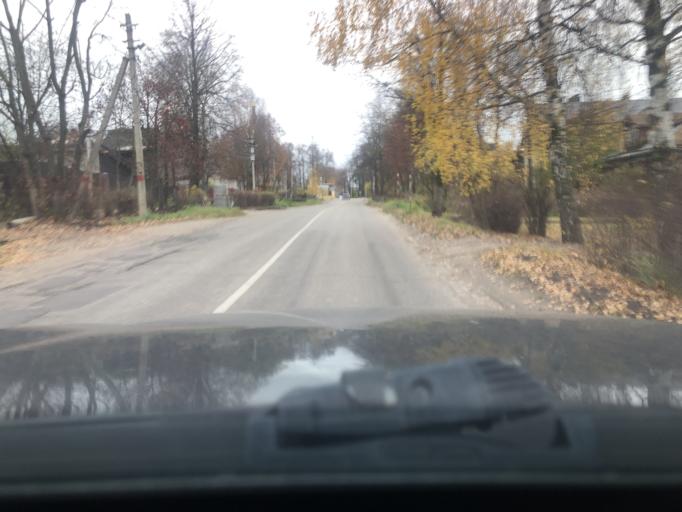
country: RU
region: Moskovskaya
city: Sergiyev Posad
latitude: 56.3015
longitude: 38.1240
